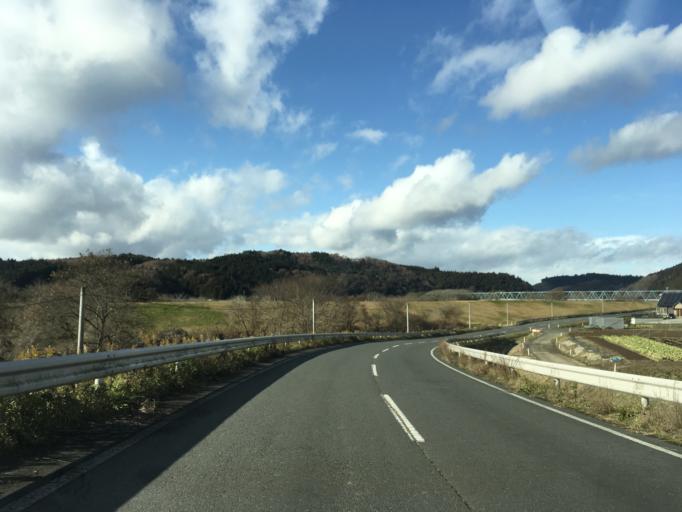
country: JP
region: Iwate
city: Ichinoseki
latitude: 38.8386
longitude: 141.2665
